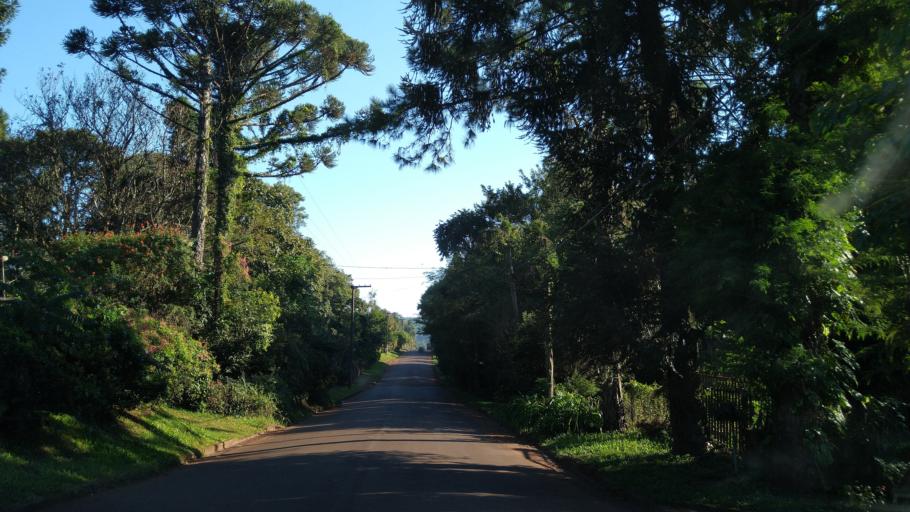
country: AR
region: Misiones
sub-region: Departamento de Montecarlo
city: Montecarlo
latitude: -26.5706
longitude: -54.7457
